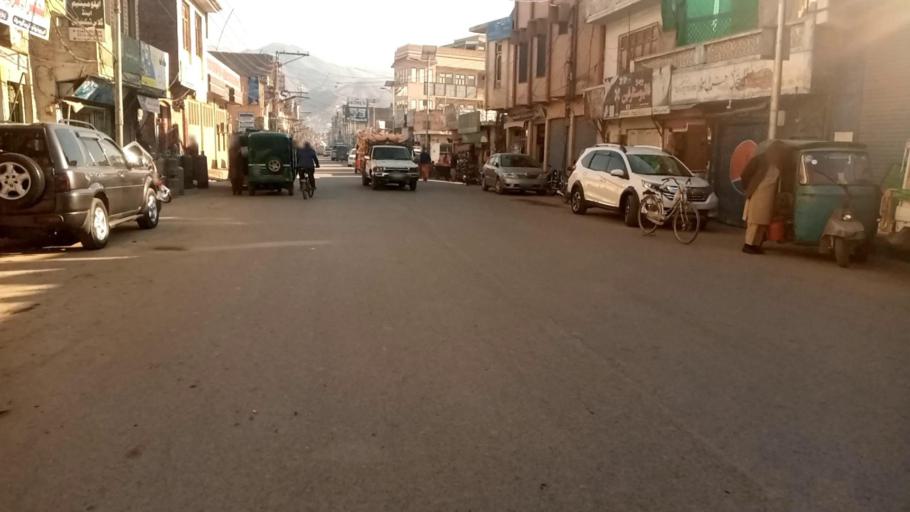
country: PK
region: Khyber Pakhtunkhwa
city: Mingora
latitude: 34.7830
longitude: 72.3544
